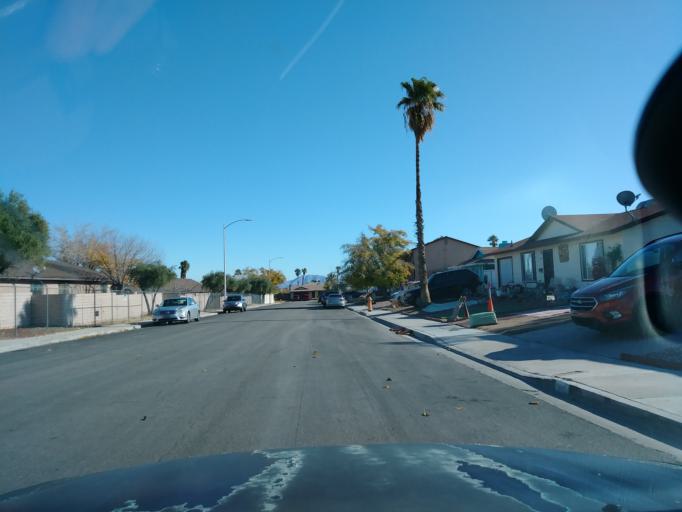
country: US
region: Nevada
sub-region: Clark County
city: Spring Valley
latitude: 36.1785
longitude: -115.2358
